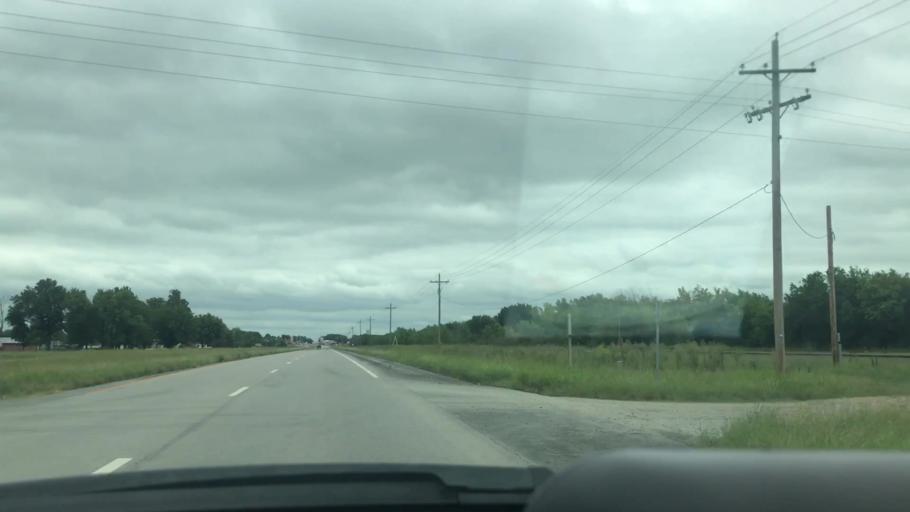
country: US
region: Oklahoma
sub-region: Mayes County
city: Pryor
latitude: 36.4233
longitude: -95.2766
